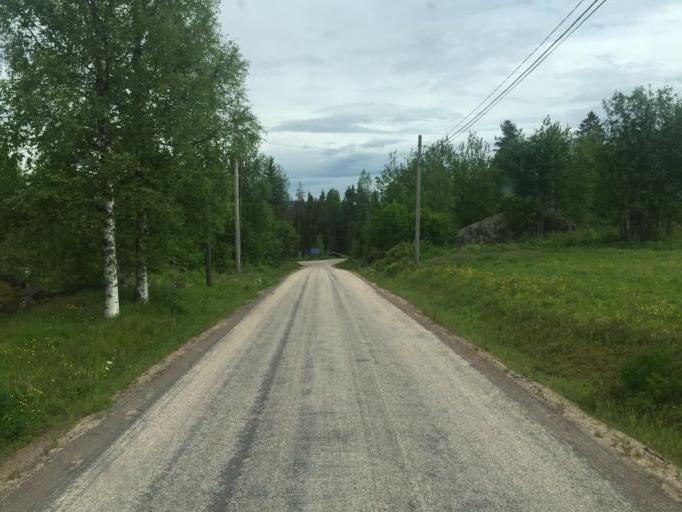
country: SE
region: Dalarna
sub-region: Malung-Saelens kommun
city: Malung
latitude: 60.3999
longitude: 13.7309
